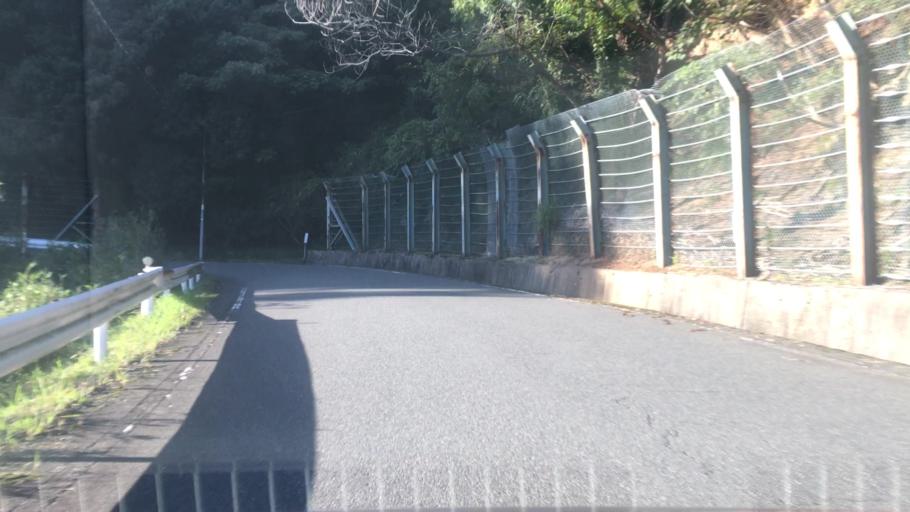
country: JP
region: Hyogo
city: Toyooka
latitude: 35.6154
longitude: 134.8764
